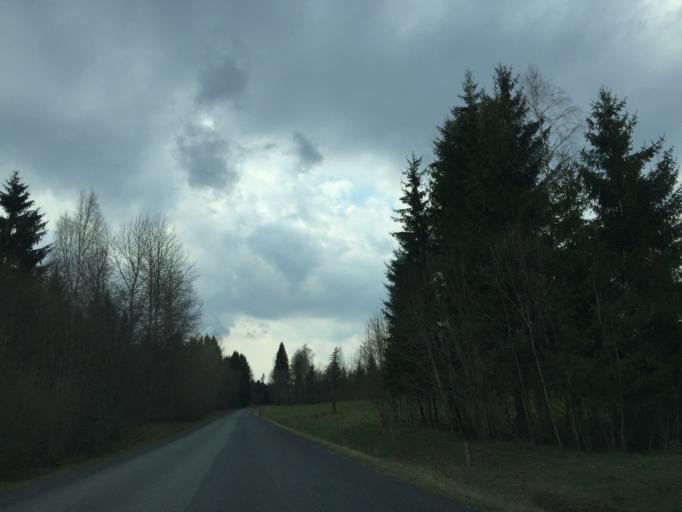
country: RU
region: Pskov
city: Pechory
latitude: 57.7337
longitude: 27.3358
